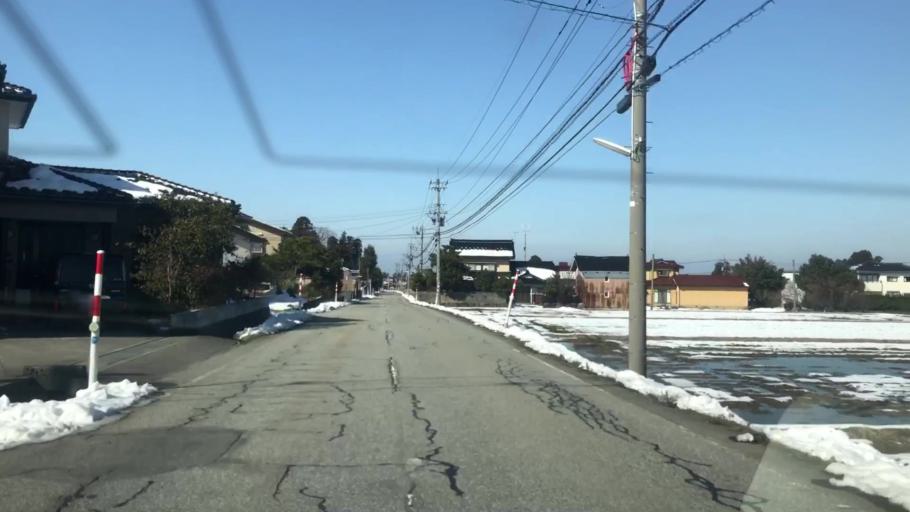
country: JP
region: Toyama
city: Toyama-shi
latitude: 36.6204
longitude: 137.2843
